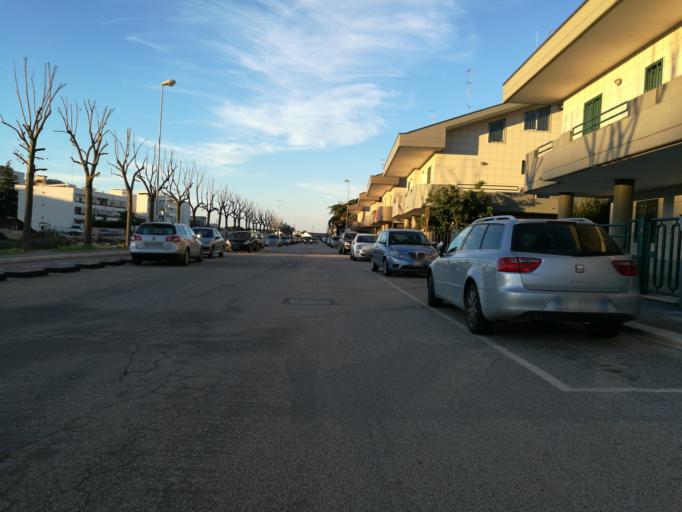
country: IT
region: Apulia
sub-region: Provincia di Bari
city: Adelfia
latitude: 41.0015
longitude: 16.8737
